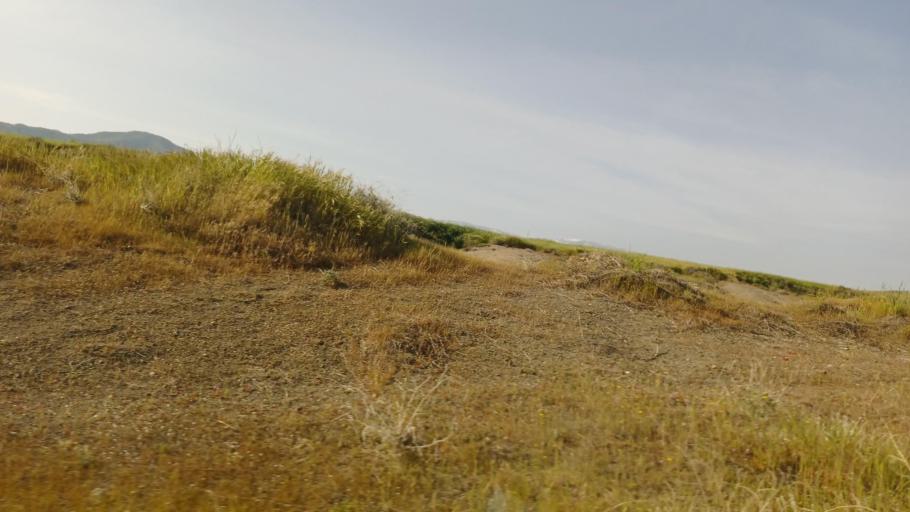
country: CY
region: Lefkosia
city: Lefka
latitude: 35.0894
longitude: 32.9452
